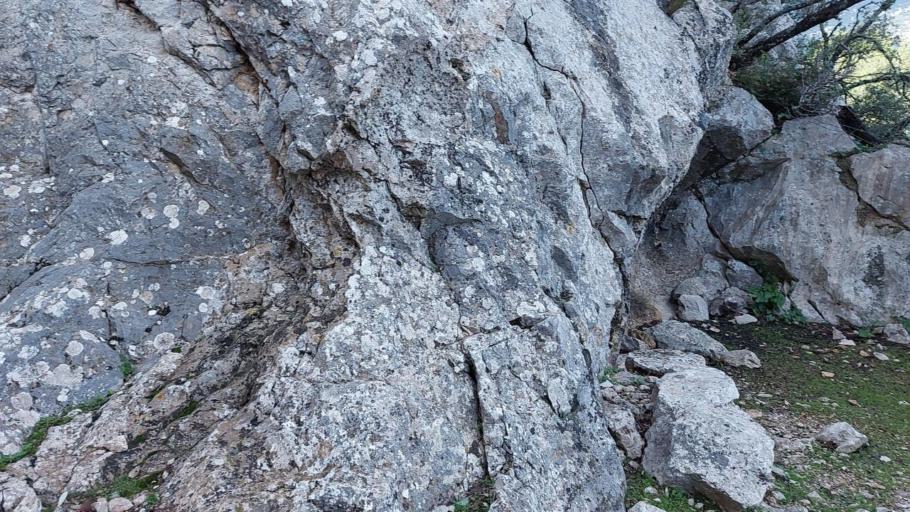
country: ES
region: Balearic Islands
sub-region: Illes Balears
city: Alaro
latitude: 39.7273
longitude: 2.7568
